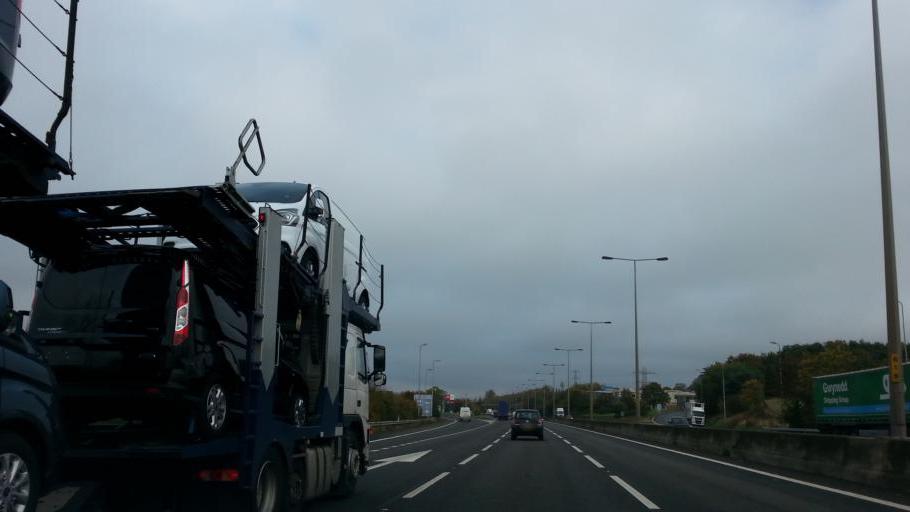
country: GB
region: England
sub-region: City and Borough of Birmingham
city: Bartley Green
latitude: 52.4258
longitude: -2.0190
